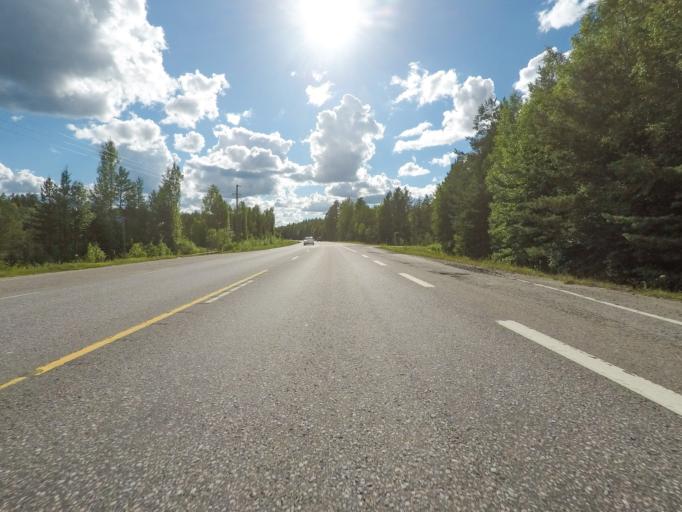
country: FI
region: Uusimaa
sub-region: Helsinki
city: Nurmijaervi
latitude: 60.5394
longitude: 24.7061
